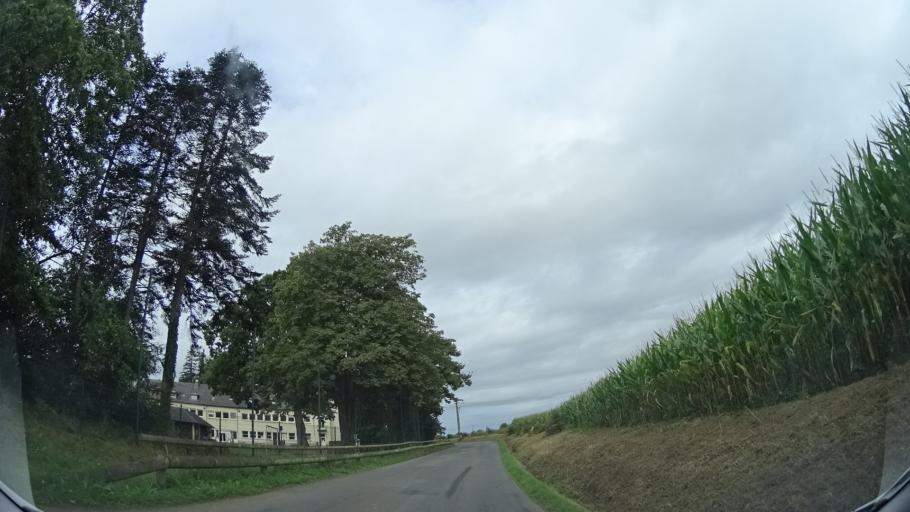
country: FR
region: Brittany
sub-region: Departement d'Ille-et-Vilaine
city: Hede-Bazouges
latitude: 48.2874
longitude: -1.8066
